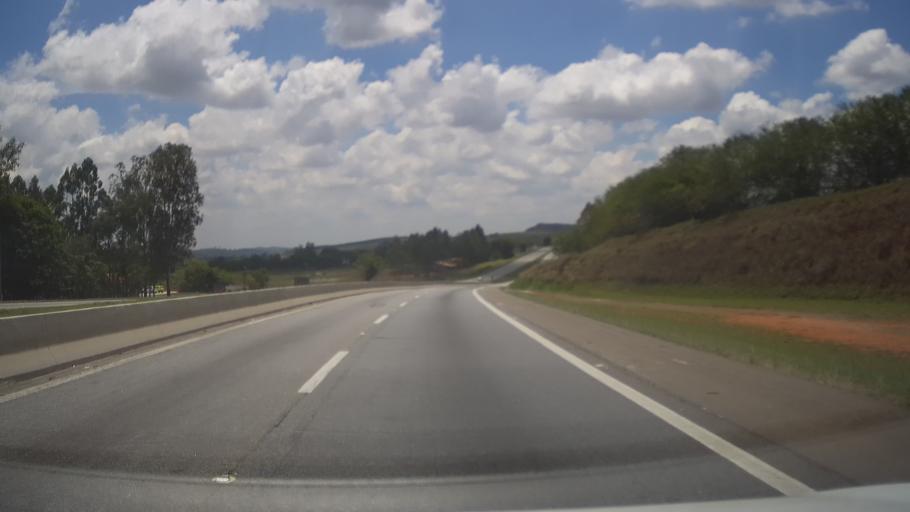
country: BR
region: Minas Gerais
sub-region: Campanha
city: Campanha
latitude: -21.7910
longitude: -45.4478
